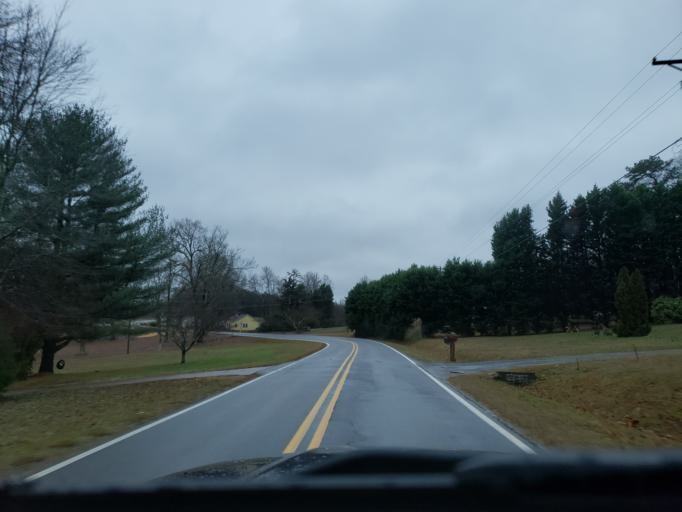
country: US
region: North Carolina
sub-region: Cleveland County
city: White Plains
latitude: 35.1917
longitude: -81.3781
